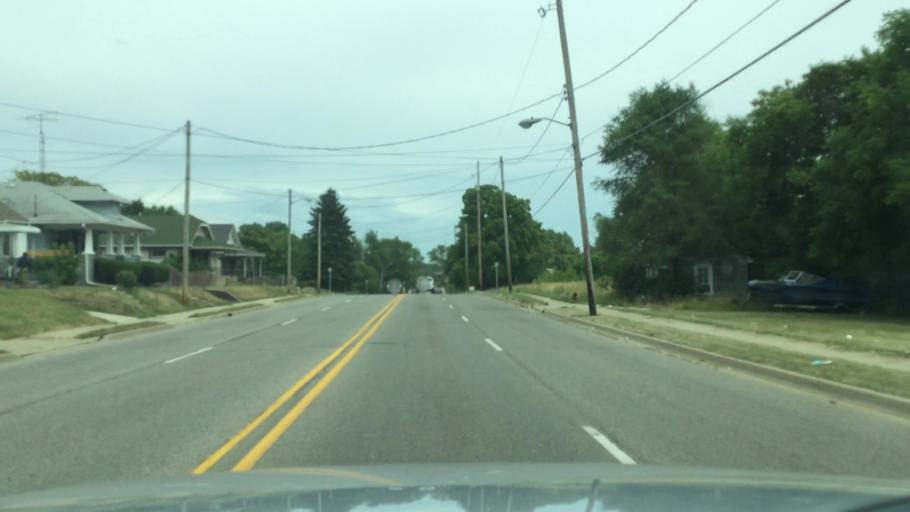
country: US
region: Michigan
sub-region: Genesee County
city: Beecher
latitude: 43.0611
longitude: -83.6901
